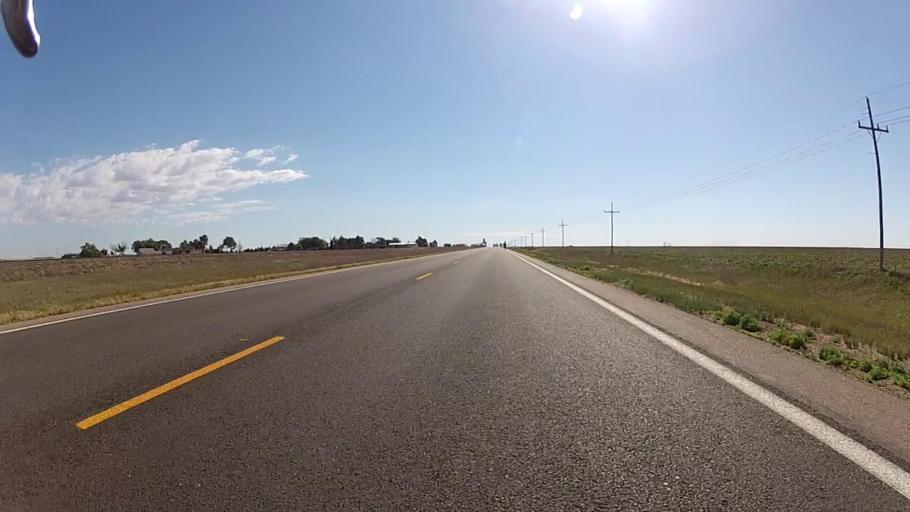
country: US
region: Kansas
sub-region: Gray County
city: Cimarron
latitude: 37.5885
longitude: -100.4815
